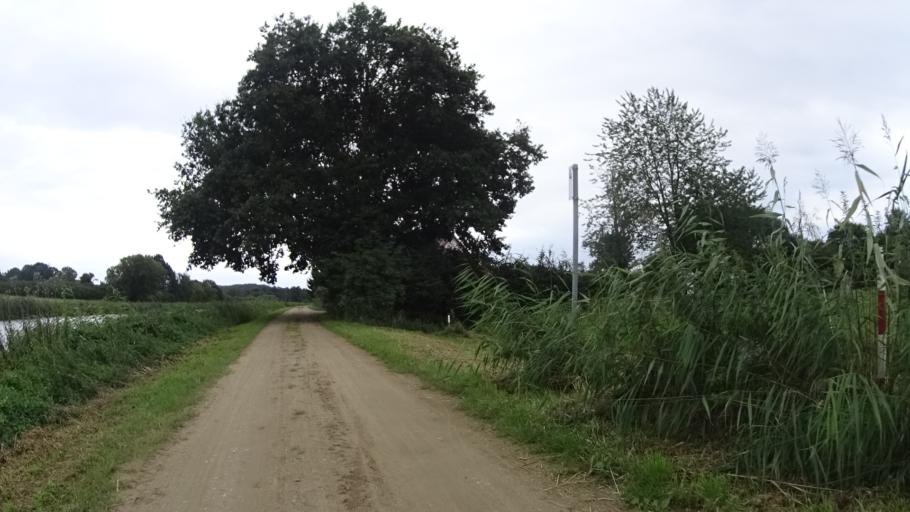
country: DE
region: Schleswig-Holstein
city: Kuhsen
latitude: 53.6837
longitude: 10.6338
